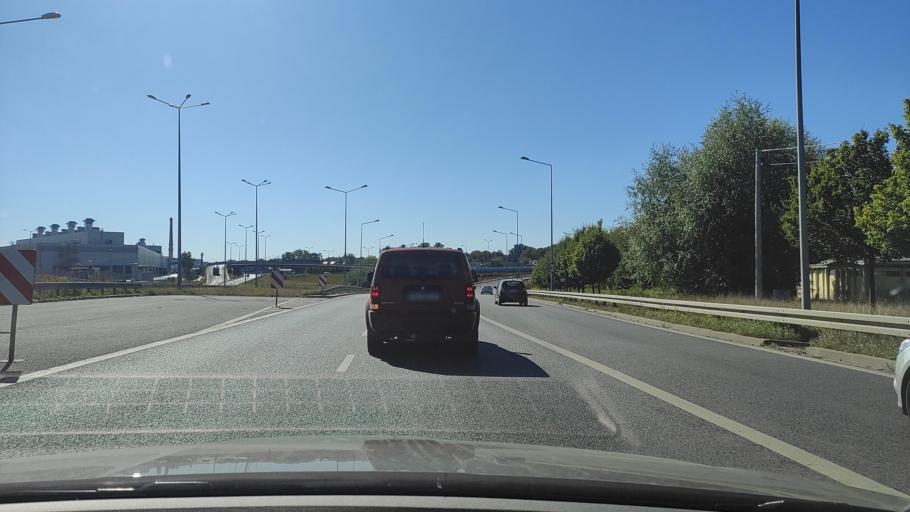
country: PL
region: Greater Poland Voivodeship
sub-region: Powiat poznanski
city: Swarzedz
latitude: 52.4136
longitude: 17.0230
